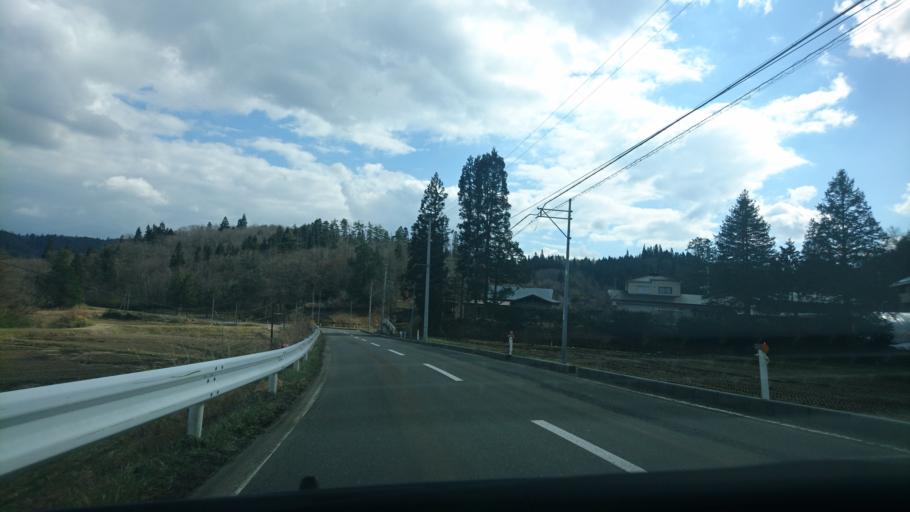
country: JP
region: Iwate
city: Hanamaki
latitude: 39.3421
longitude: 141.2359
